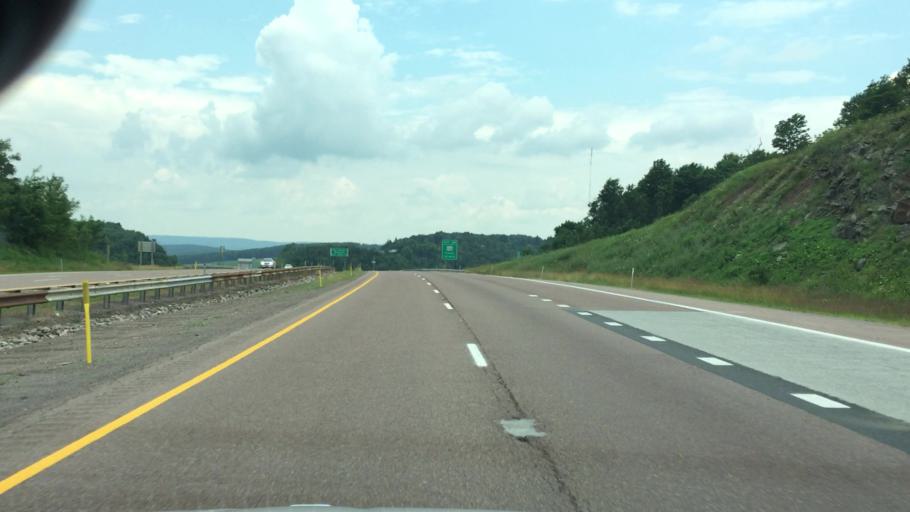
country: US
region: Maryland
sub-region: Allegany County
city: Frostburg
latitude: 39.6746
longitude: -78.9632
